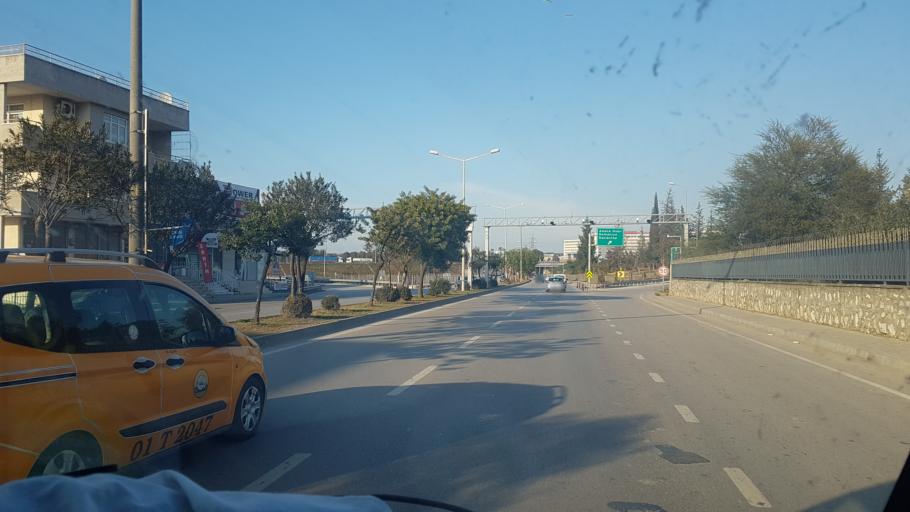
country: TR
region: Adana
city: Adana
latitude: 37.0204
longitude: 35.3421
